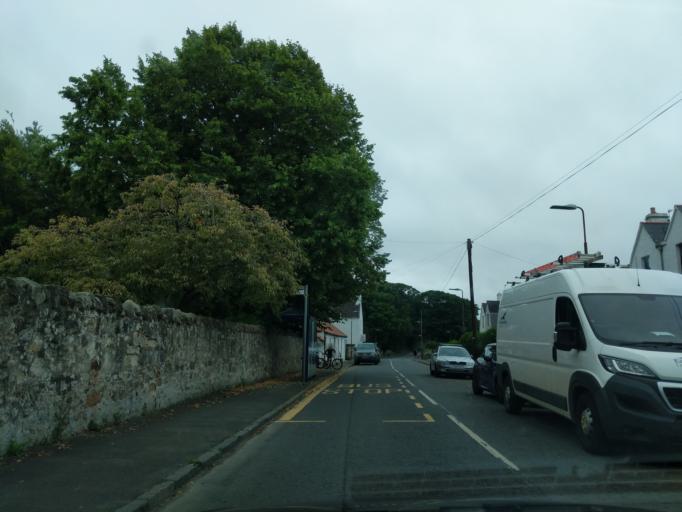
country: GB
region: Scotland
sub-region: East Lothian
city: Pencaitland
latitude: 55.9089
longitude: -2.8941
